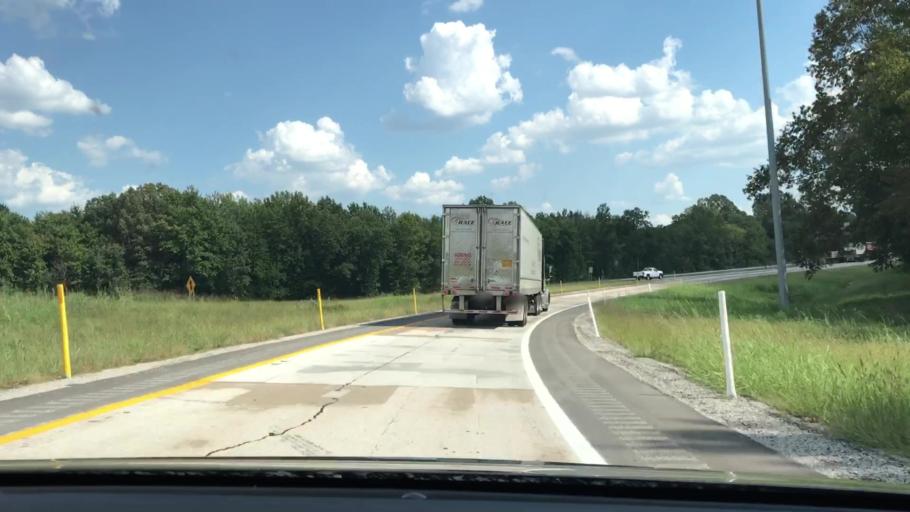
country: US
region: Kentucky
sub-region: Ohio County
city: Oak Grove
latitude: 37.3817
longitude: -86.8085
